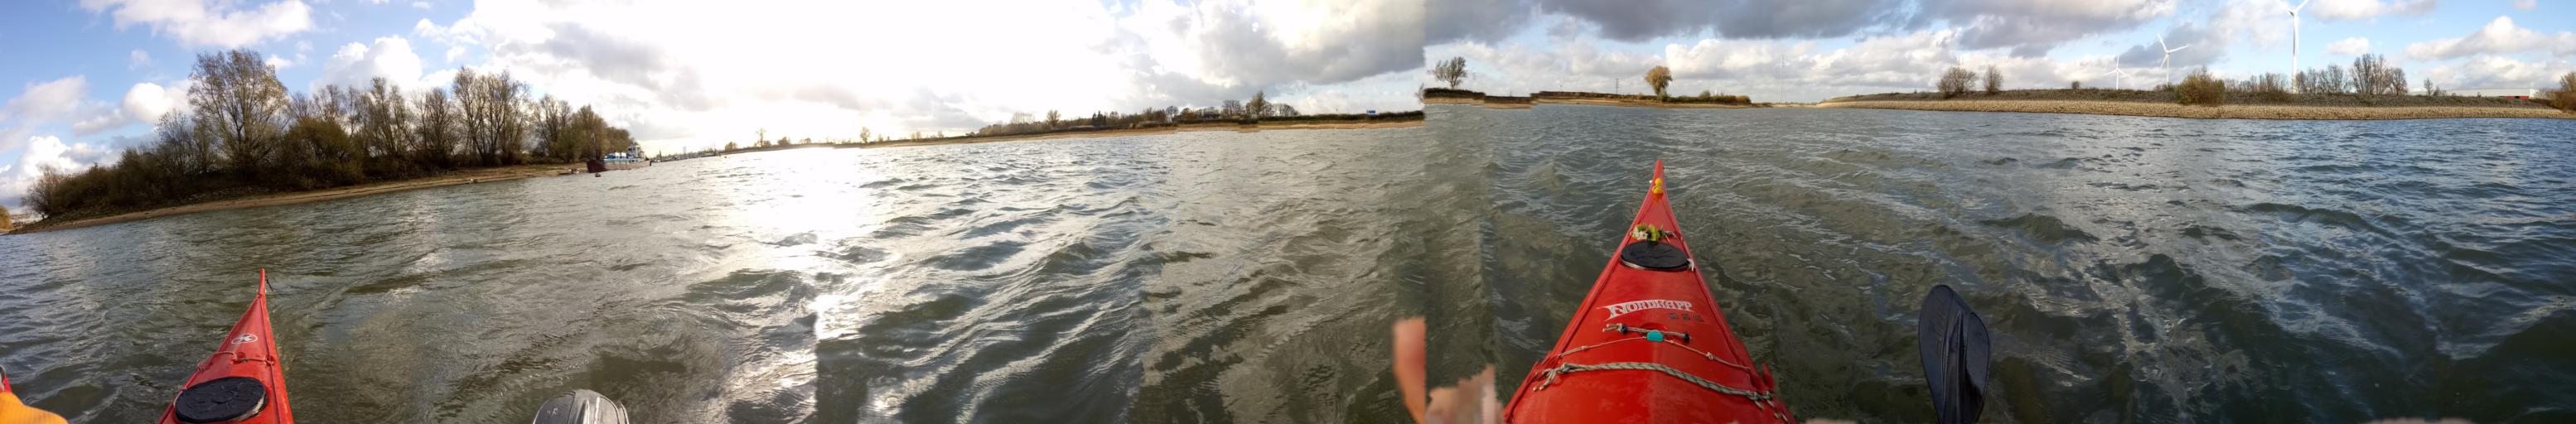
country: NL
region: Gelderland
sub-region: Gemeente Zutphen
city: Zutphen
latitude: 52.1564
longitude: 6.1868
